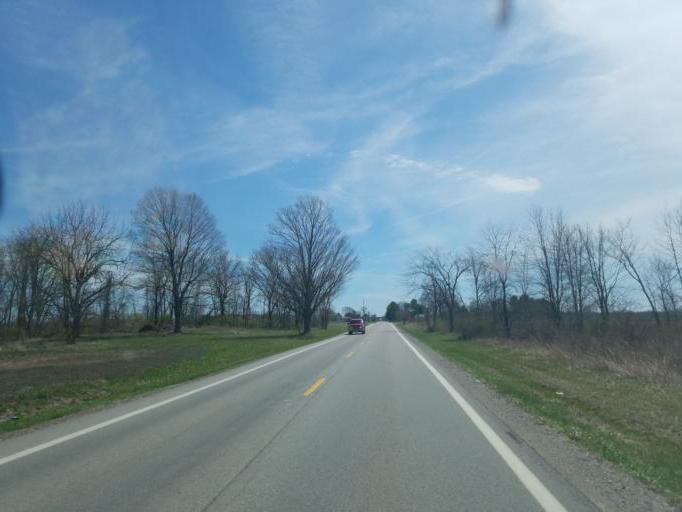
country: US
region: Ohio
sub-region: Delaware County
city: Ashley
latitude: 40.4298
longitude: -83.0427
